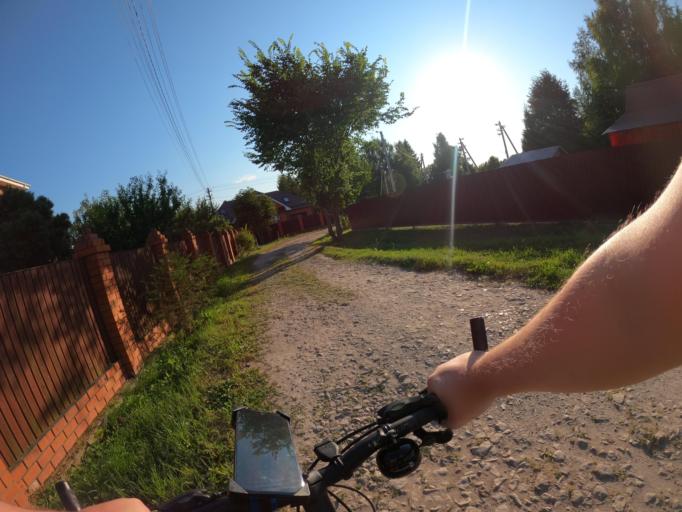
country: RU
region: Moskovskaya
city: Beloozerskiy
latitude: 55.4897
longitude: 38.4342
